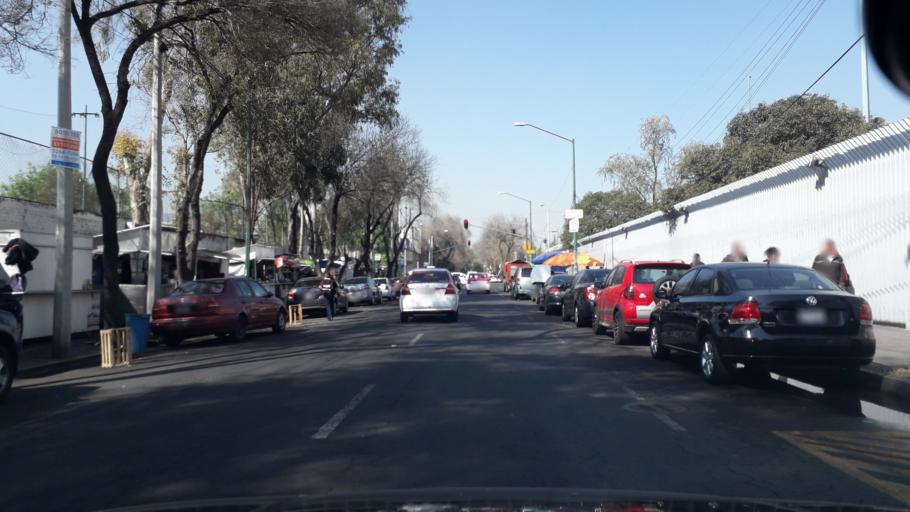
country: MX
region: Mexico City
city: Cuauhtemoc
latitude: 19.4440
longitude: -99.1514
